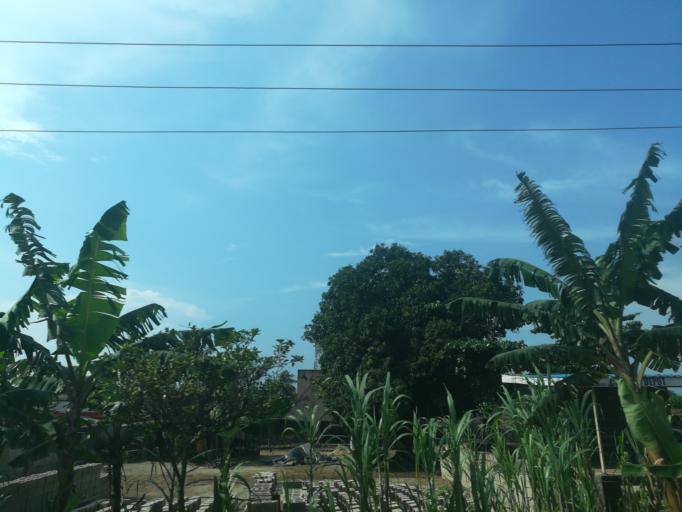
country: NG
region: Lagos
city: Ikorodu
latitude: 6.6305
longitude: 3.5181
